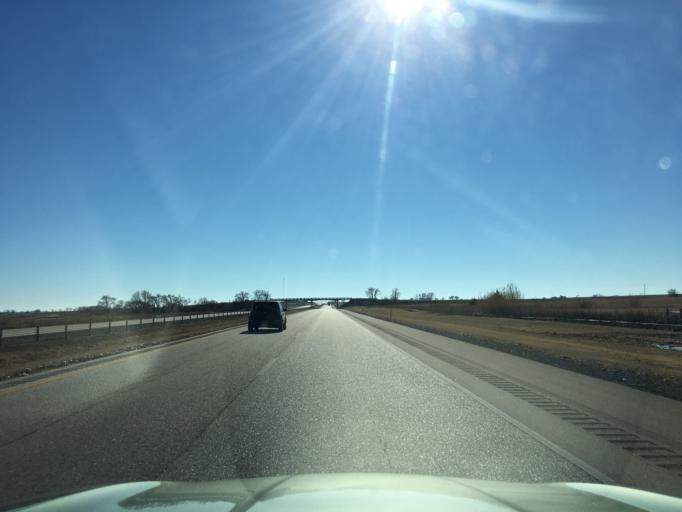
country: US
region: Oklahoma
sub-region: Kay County
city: Blackwell
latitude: 36.8875
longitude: -97.3527
